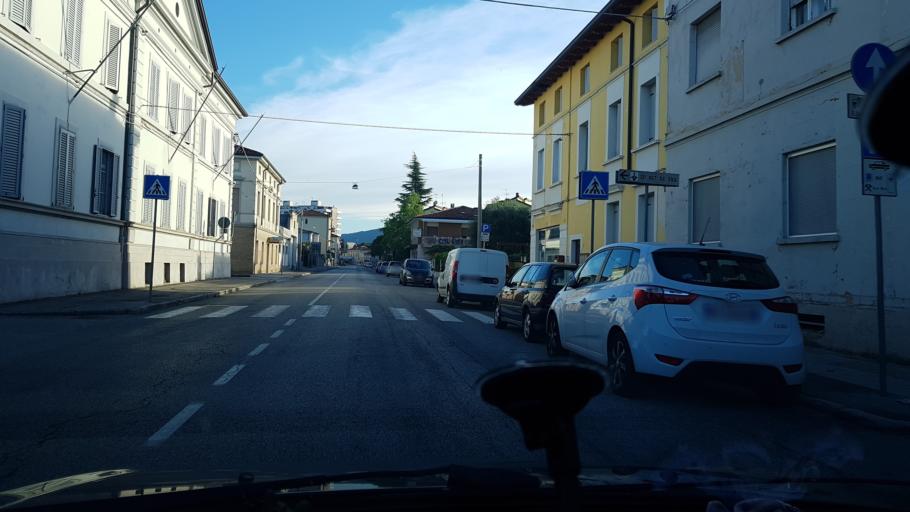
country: IT
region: Friuli Venezia Giulia
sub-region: Provincia di Gorizia
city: Gorizia
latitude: 45.9324
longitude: 13.6131
